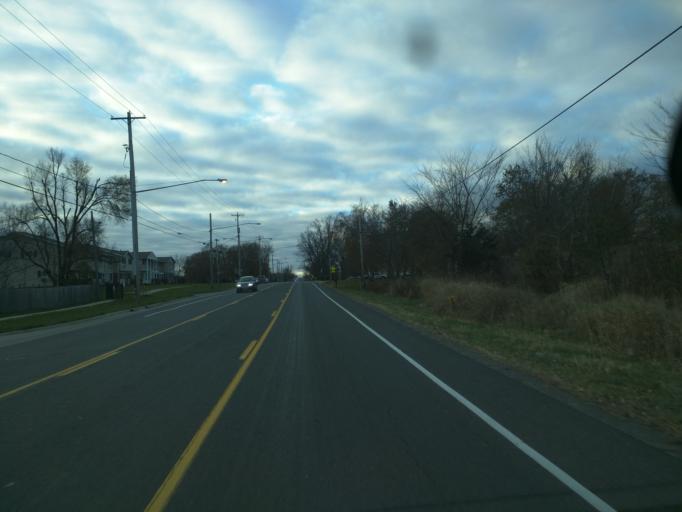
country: US
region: Michigan
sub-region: Eaton County
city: Dimondale
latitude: 42.6725
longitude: -84.6031
